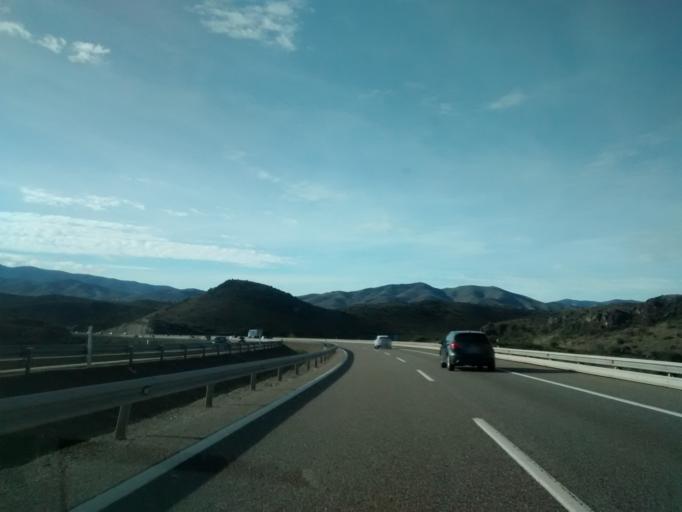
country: ES
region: Aragon
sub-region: Provincia de Zaragoza
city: Morata de Jalon
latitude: 41.4846
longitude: -1.4427
